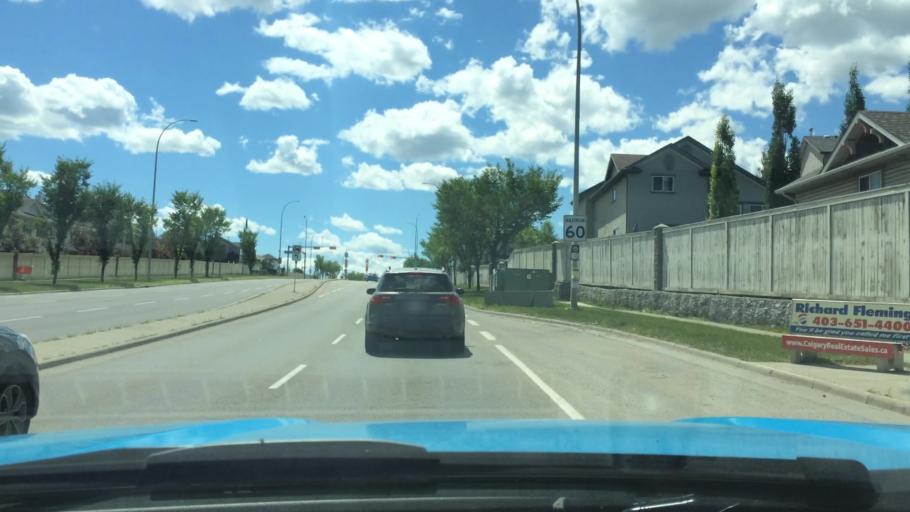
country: CA
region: Alberta
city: Calgary
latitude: 51.1529
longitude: -114.0674
